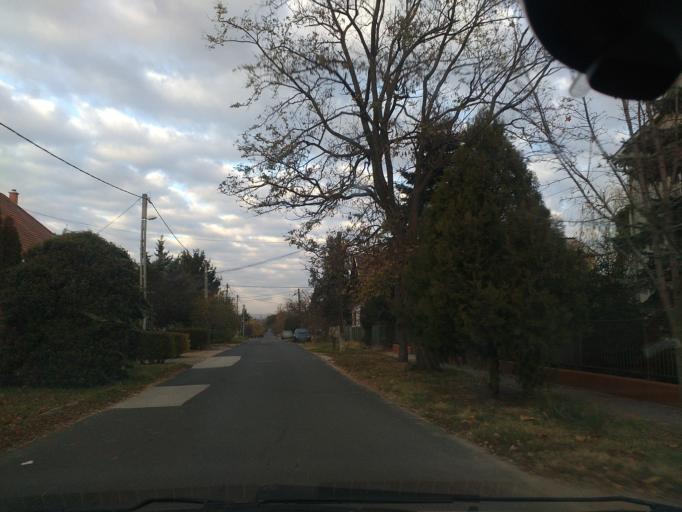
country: HU
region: Budapest
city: Budapest XVIII. keruelet
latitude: 47.4334
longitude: 19.2125
